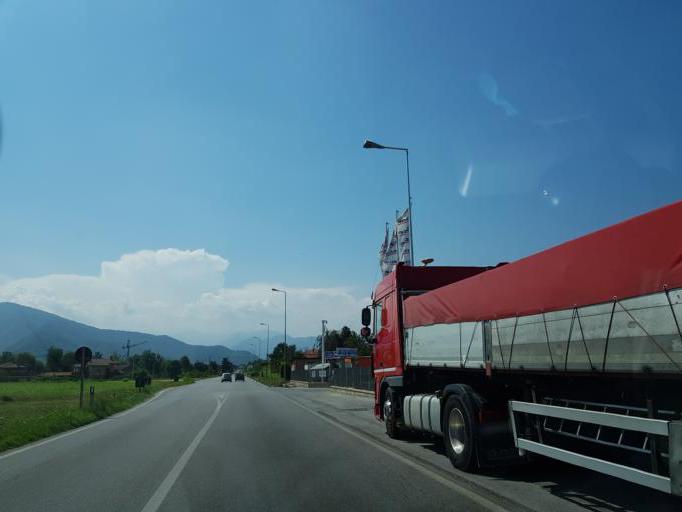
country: IT
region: Piedmont
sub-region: Provincia di Cuneo
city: San Rocco
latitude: 44.3984
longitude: 7.4671
